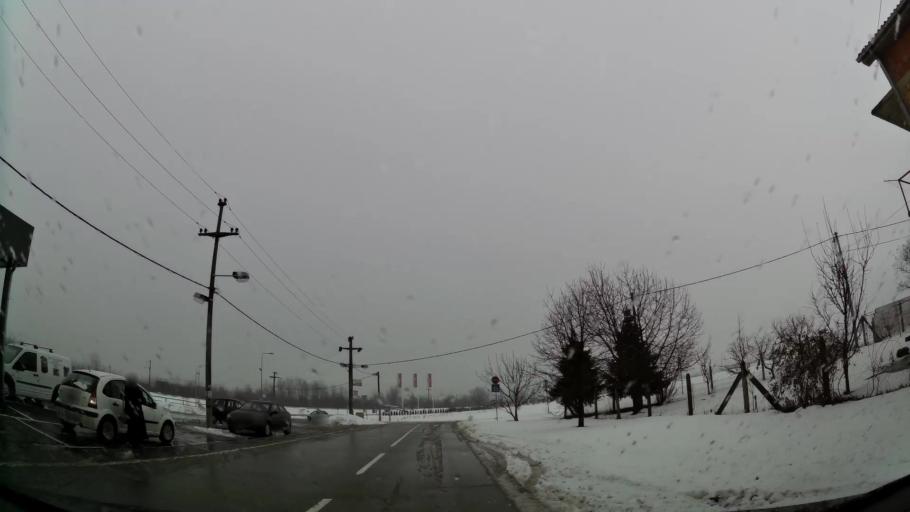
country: RS
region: Central Serbia
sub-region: Belgrade
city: Zemun
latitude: 44.8455
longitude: 20.3473
